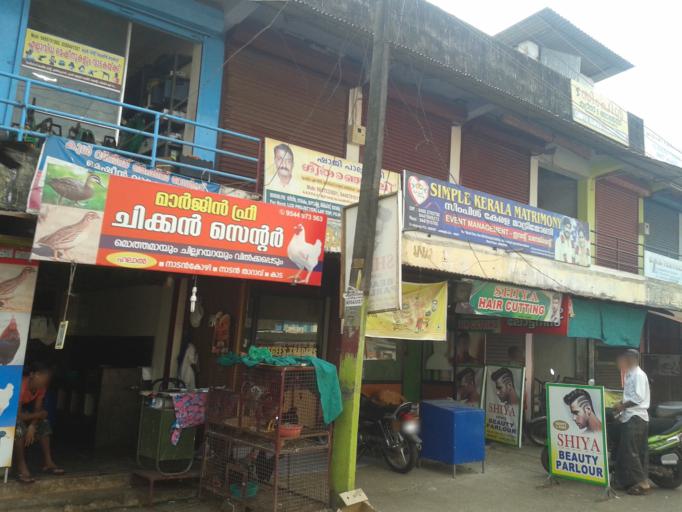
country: IN
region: Kerala
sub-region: Thrissur District
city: Kizhake Chalakudi
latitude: 10.3064
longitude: 76.3396
